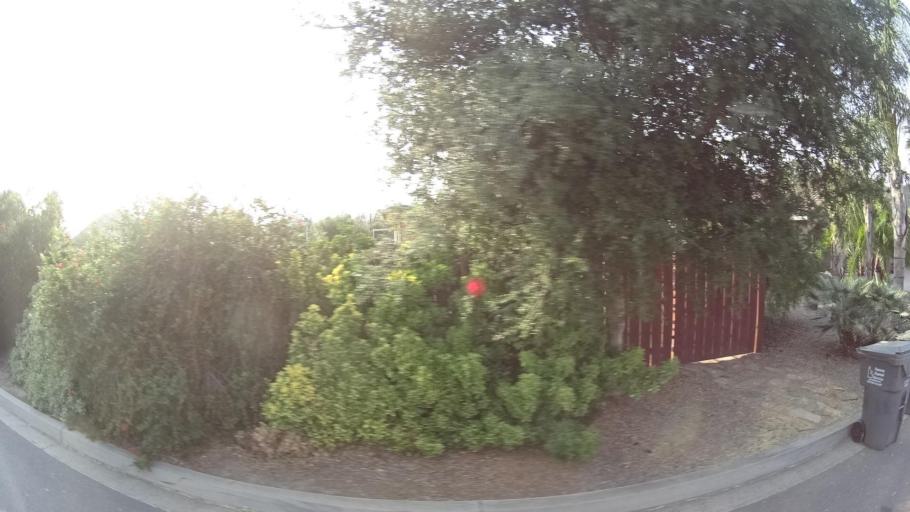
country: US
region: California
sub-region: San Diego County
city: San Diego Country Estates
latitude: 33.0076
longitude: -116.8213
